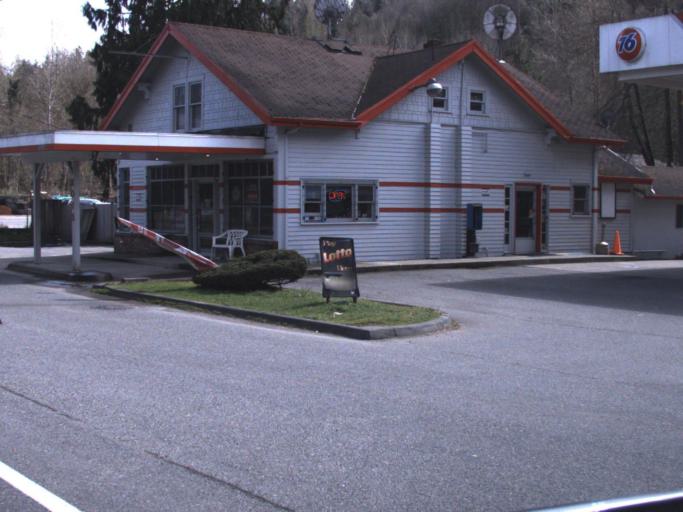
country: US
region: Washington
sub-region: King County
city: Maple Heights-Lake Desire
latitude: 47.4627
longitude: -122.1014
